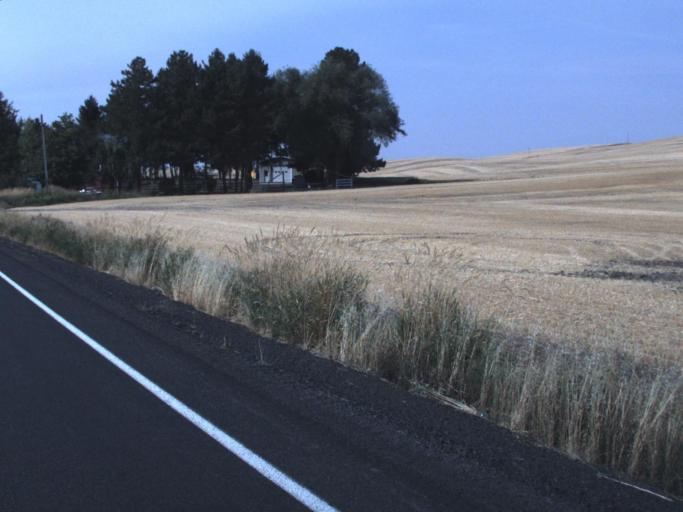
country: US
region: Washington
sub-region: Whitman County
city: Pullman
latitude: 46.7975
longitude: -117.1360
